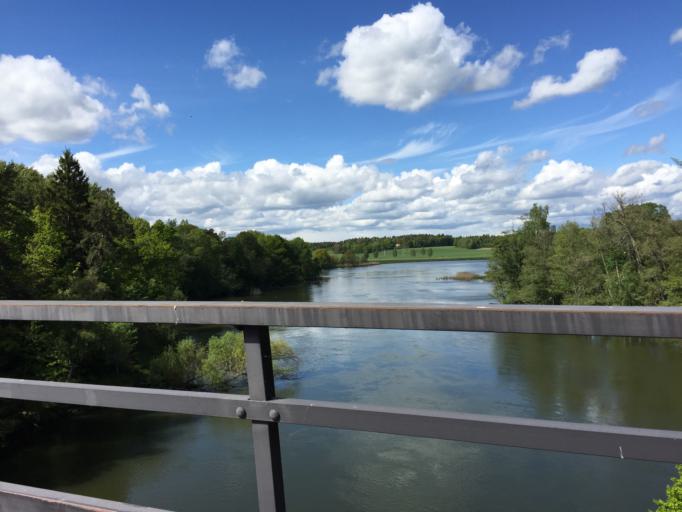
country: SE
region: OEstergoetland
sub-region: Norrkopings Kommun
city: Kimstad
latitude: 58.5193
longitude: 15.9682
